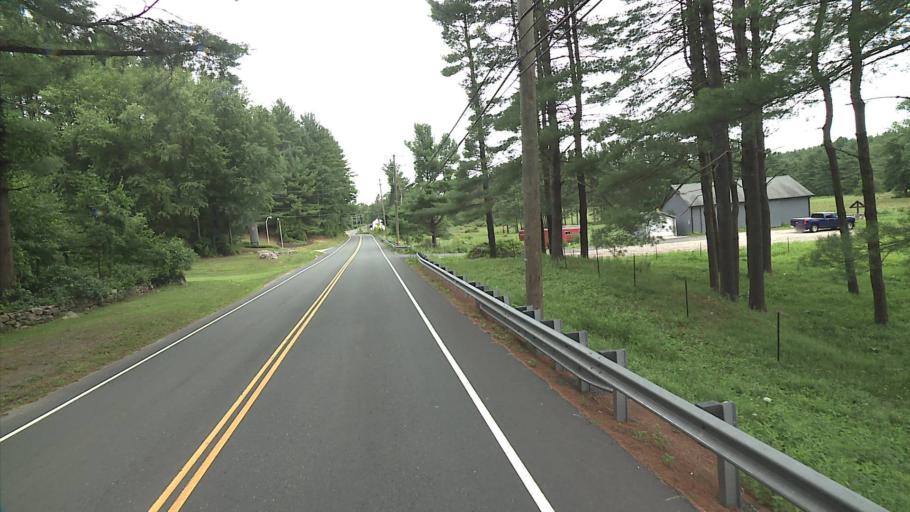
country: US
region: Connecticut
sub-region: Litchfield County
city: Winsted
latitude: 41.9568
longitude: -73.0485
